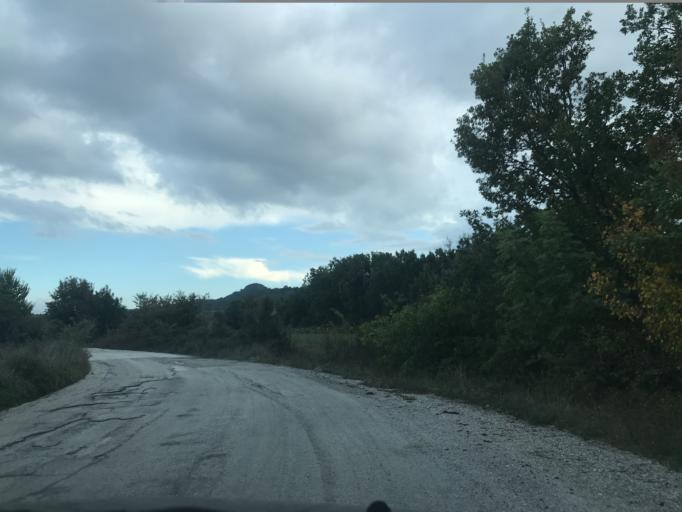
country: IT
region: Molise
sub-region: Provincia di Campobasso
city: Duronia
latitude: 41.6754
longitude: 14.4529
